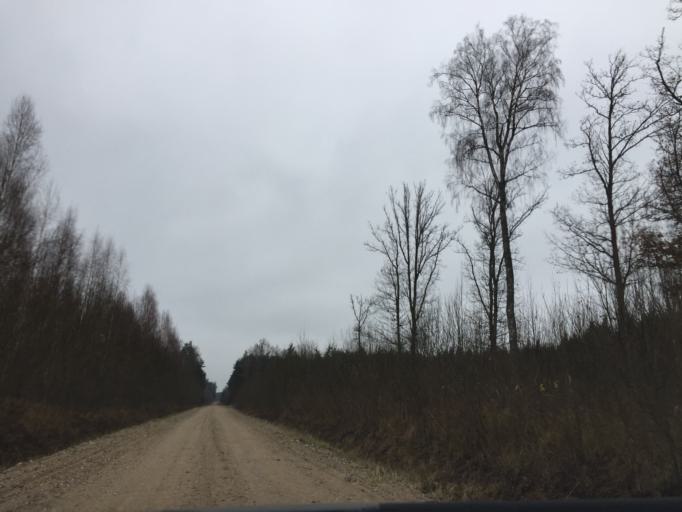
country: LV
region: Limbazu Rajons
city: Limbazi
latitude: 57.4799
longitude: 24.7534
